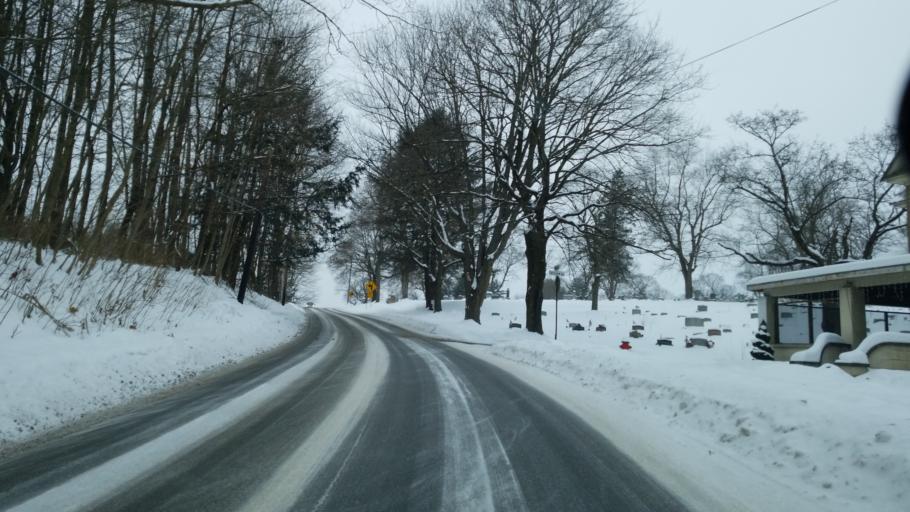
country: US
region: Pennsylvania
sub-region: Clearfield County
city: Clearfield
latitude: 41.0253
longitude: -78.4295
